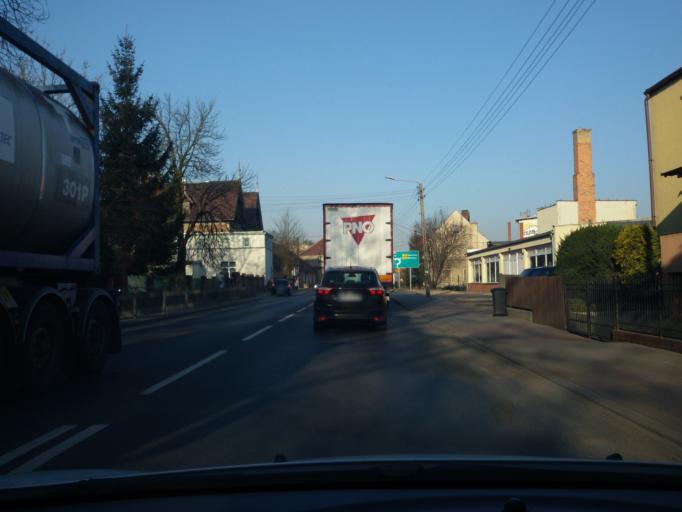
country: PL
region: Lubusz
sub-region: Powiat wschowski
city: Wschowa
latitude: 51.8014
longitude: 16.3180
